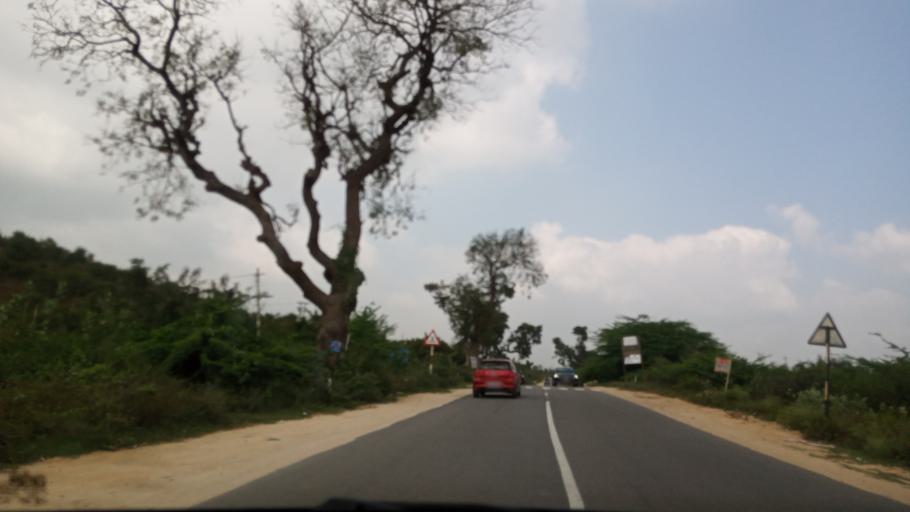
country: IN
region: Andhra Pradesh
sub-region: Chittoor
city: Madanapalle
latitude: 13.5885
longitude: 78.5255
